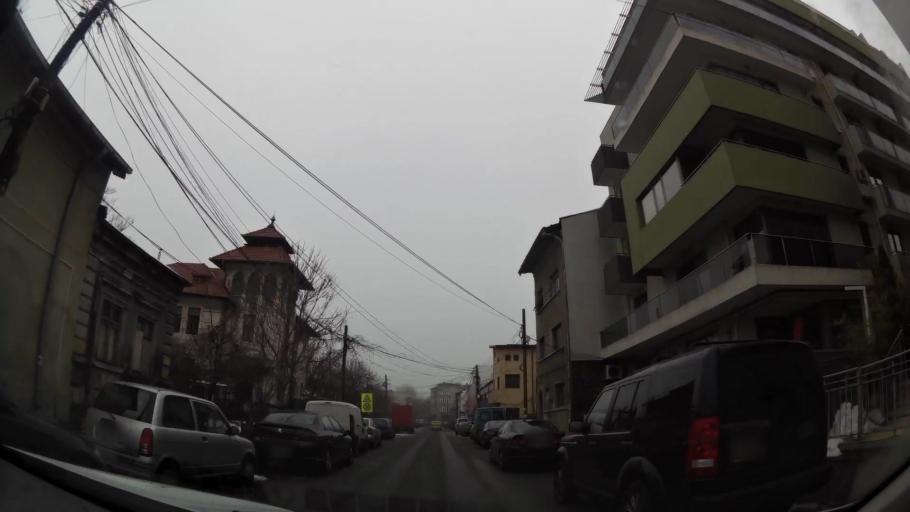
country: RO
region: Bucuresti
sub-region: Municipiul Bucuresti
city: Bucharest
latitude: 44.4384
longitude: 26.1317
